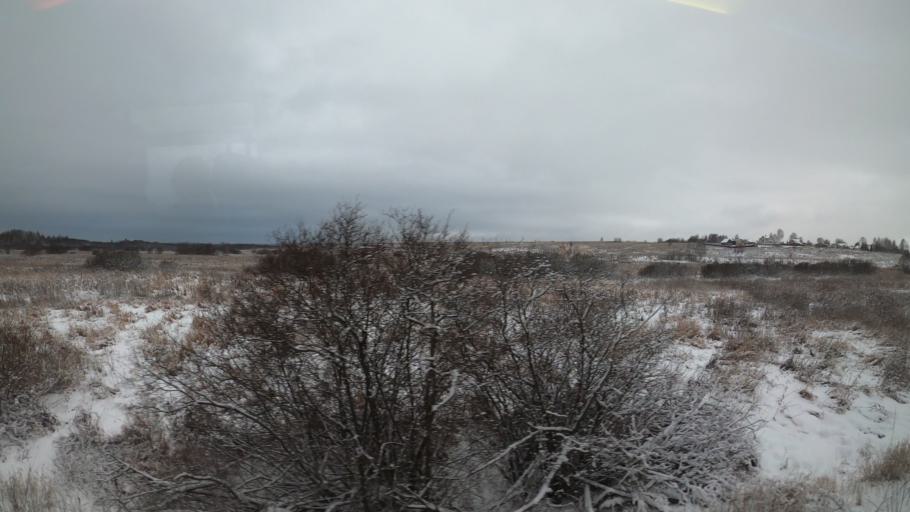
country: RU
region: Jaroslavl
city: Pereslavl'-Zalesskiy
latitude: 56.6980
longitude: 38.9162
